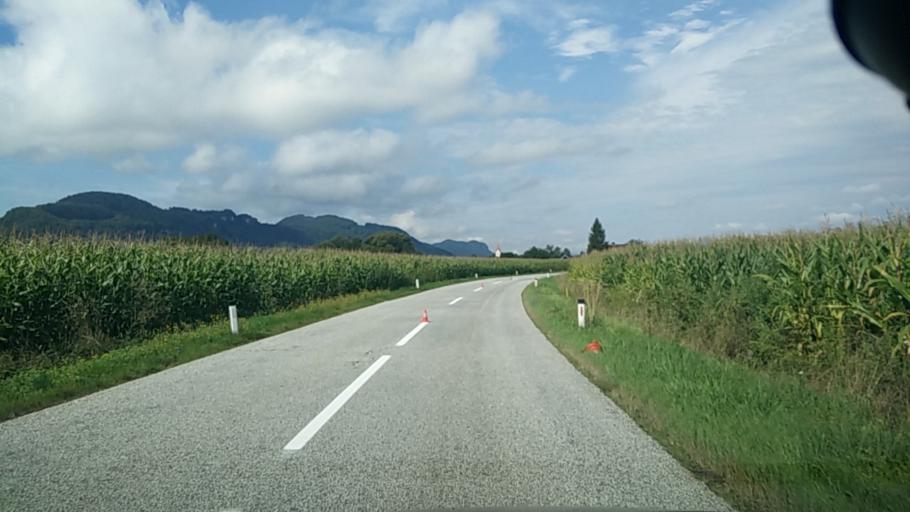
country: AT
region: Carinthia
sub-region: Politischer Bezirk Klagenfurt Land
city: Grafenstein
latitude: 46.6127
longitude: 14.4994
